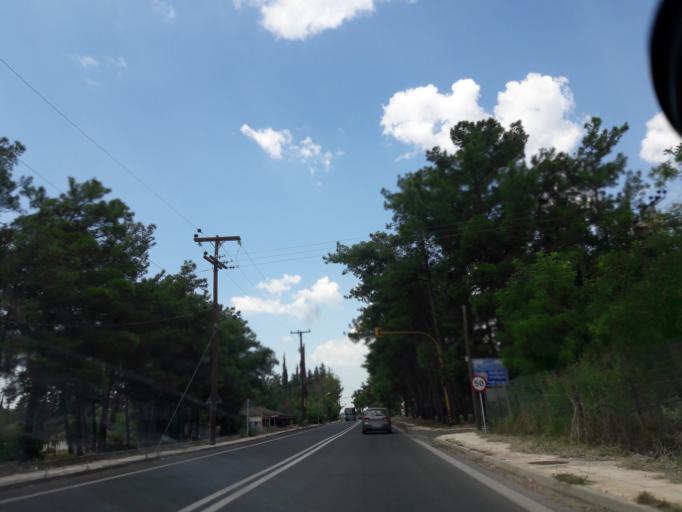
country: GR
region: Central Macedonia
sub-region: Nomos Thessalonikis
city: Souroti
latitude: 40.5123
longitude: 23.0778
